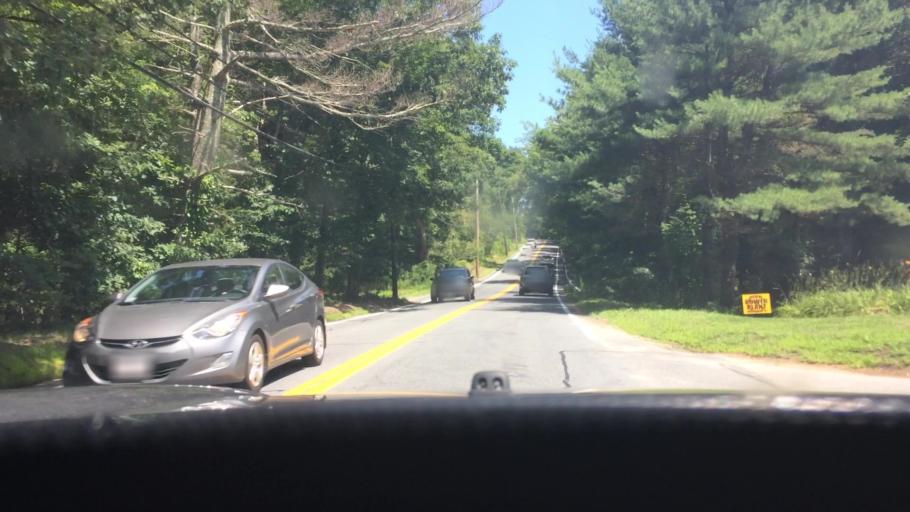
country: US
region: Rhode Island
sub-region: Providence County
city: Harrisville
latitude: 41.9698
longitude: -71.6594
